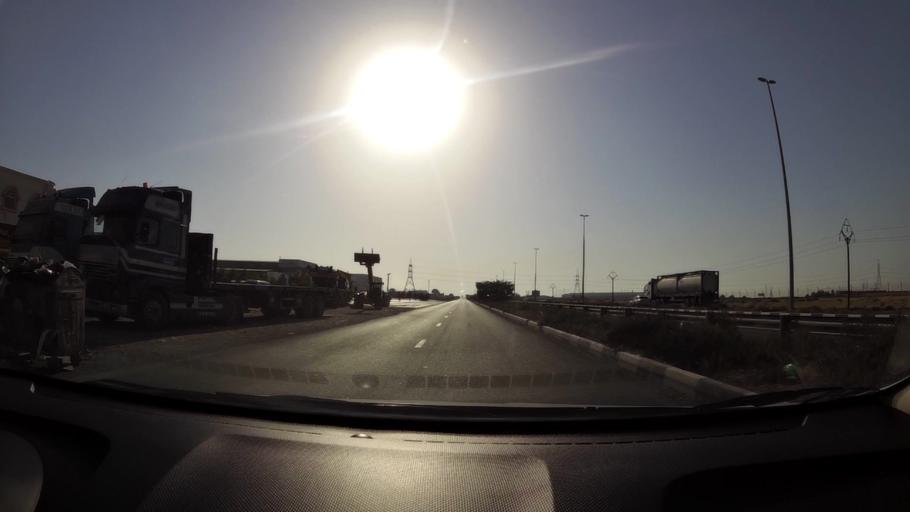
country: AE
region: Ajman
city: Ajman
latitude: 25.4433
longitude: 55.5446
